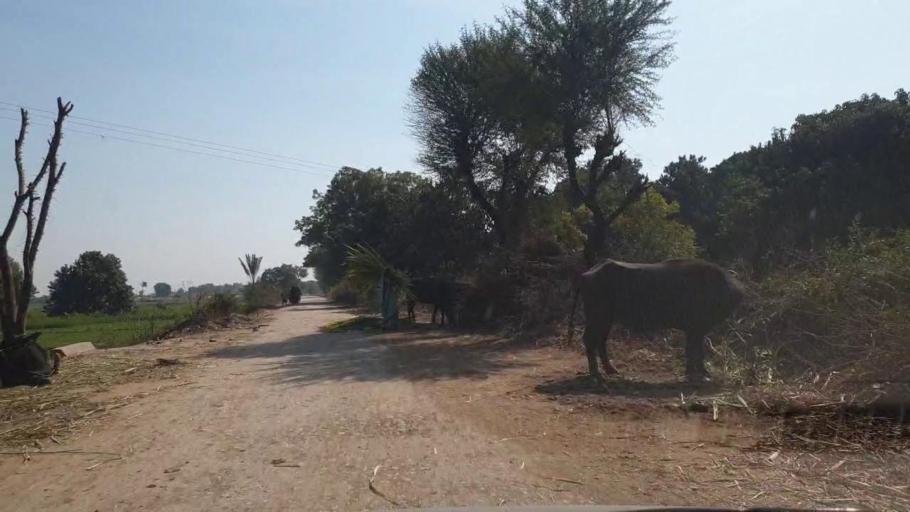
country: PK
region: Sindh
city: Tando Allahyar
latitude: 25.3870
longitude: 68.7814
